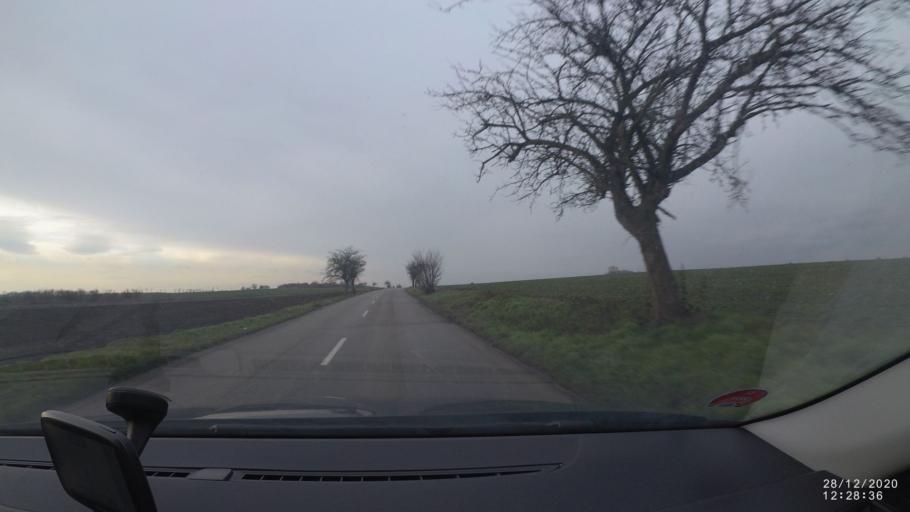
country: CZ
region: Central Bohemia
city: Brandys nad Labem-Stara Boleslav
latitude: 50.1958
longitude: 14.6277
